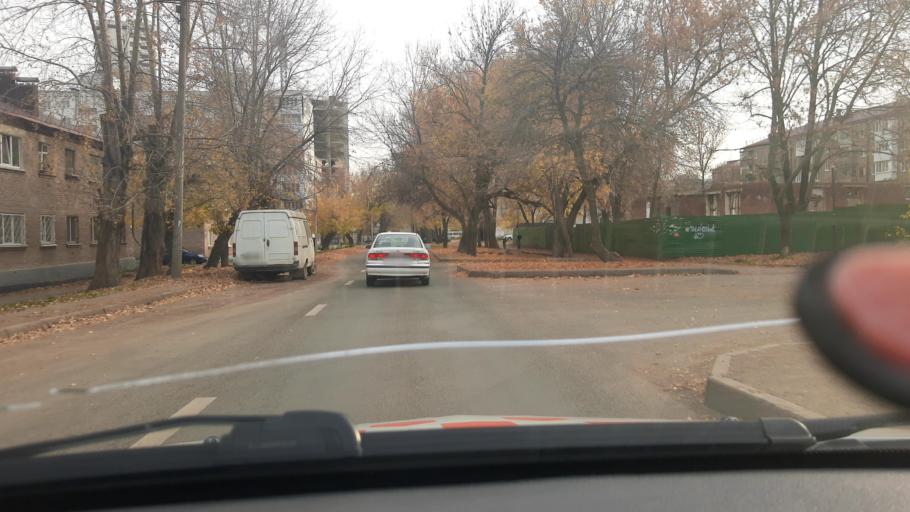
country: RU
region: Bashkortostan
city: Ufa
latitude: 54.8090
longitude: 56.1268
